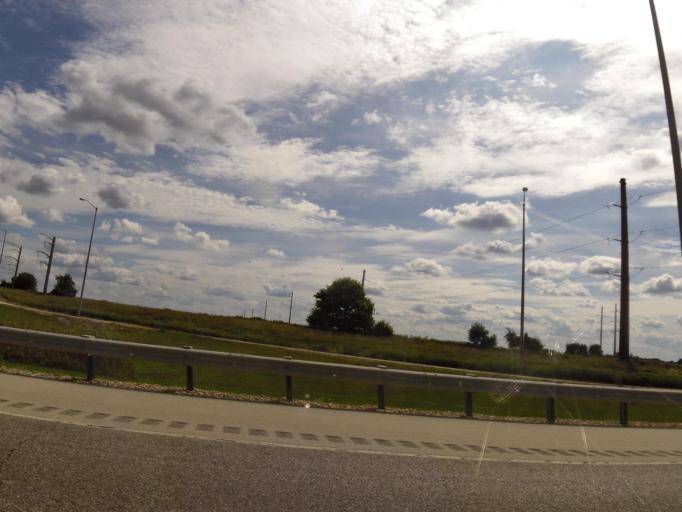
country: US
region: Illinois
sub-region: DeKalb County
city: DeKalb
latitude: 41.9018
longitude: -88.7434
